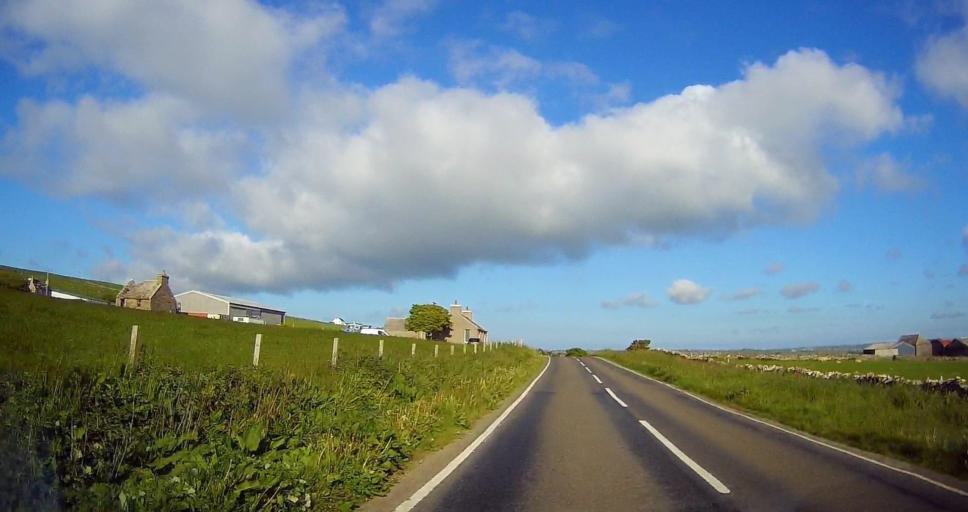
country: GB
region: Scotland
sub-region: Orkney Islands
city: Orkney
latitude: 58.9794
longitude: -3.0258
